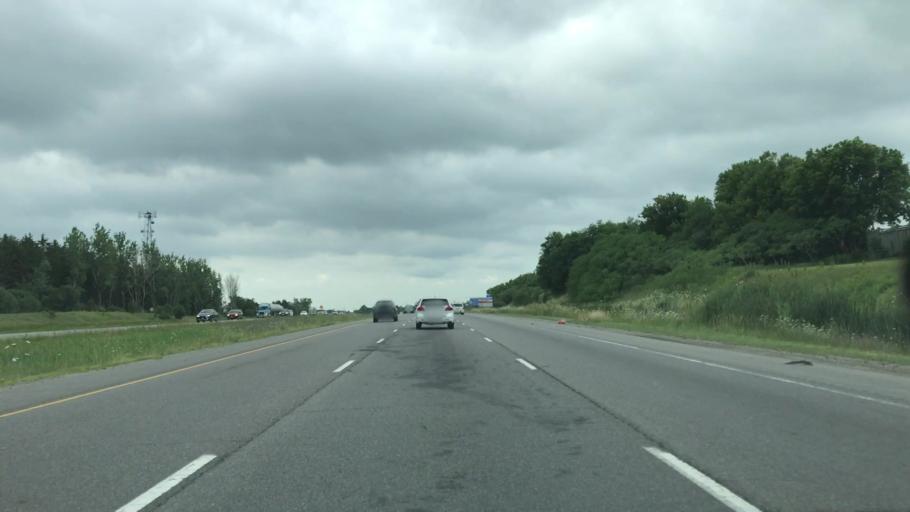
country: CA
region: Ontario
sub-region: York
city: Richmond Hill
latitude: 43.9578
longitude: -79.3931
